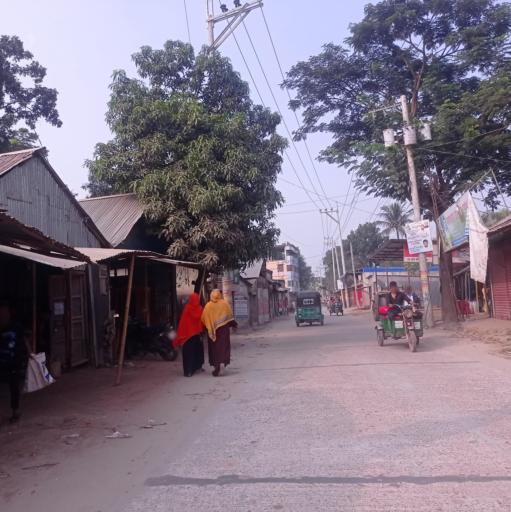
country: BD
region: Dhaka
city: Bhairab Bazar
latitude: 24.1007
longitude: 90.8526
